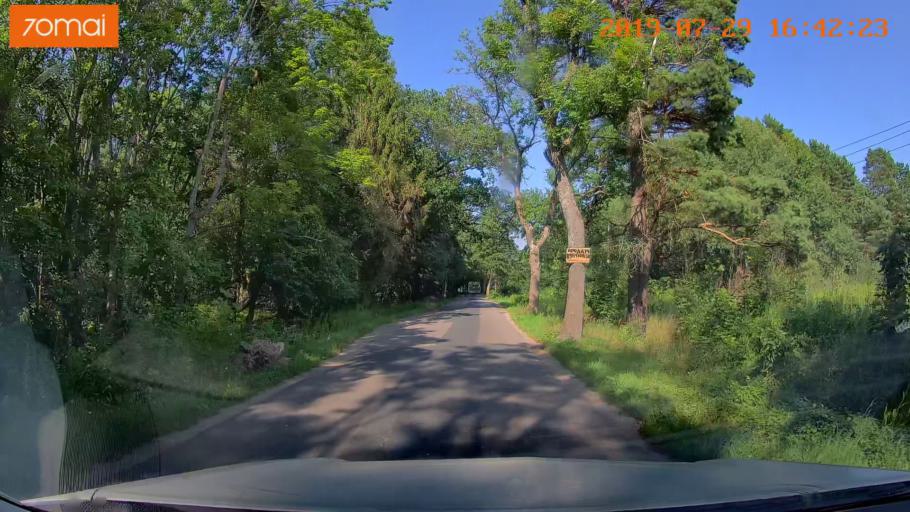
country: RU
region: Kaliningrad
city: Primorsk
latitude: 54.7425
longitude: 20.0726
